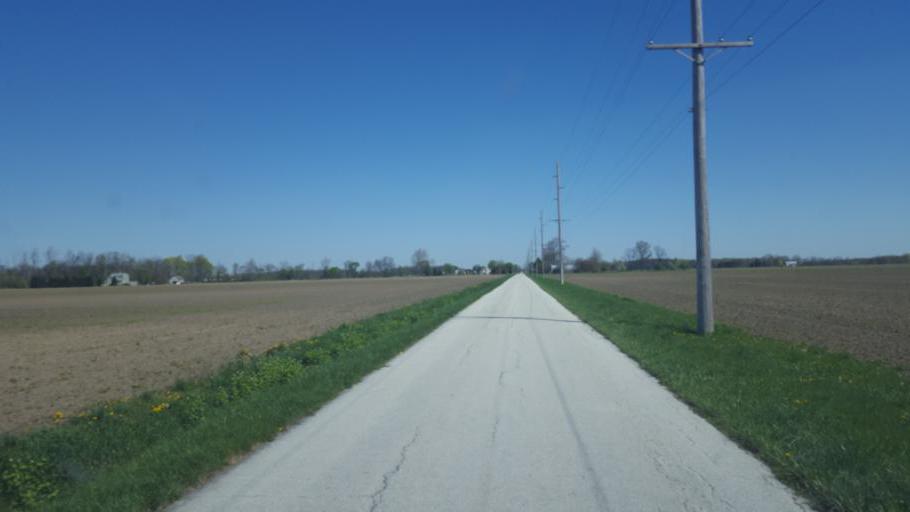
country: US
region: Ohio
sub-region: Sandusky County
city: Ballville
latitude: 41.2347
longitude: -83.1871
